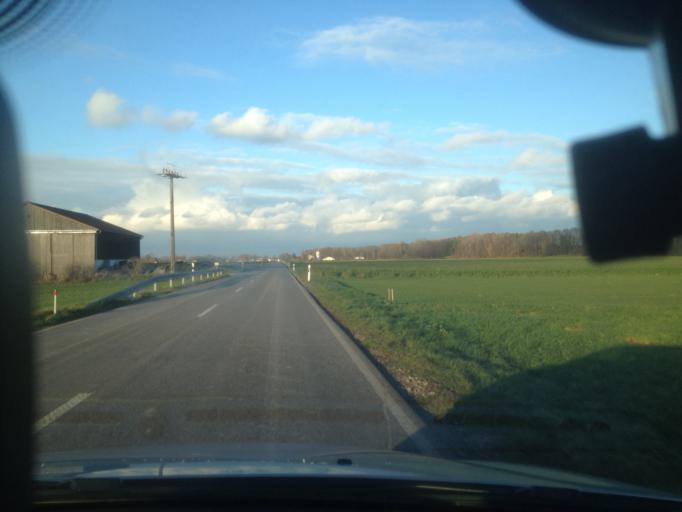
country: DE
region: Bavaria
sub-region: Upper Bavaria
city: Prittriching
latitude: 48.2158
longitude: 10.9345
